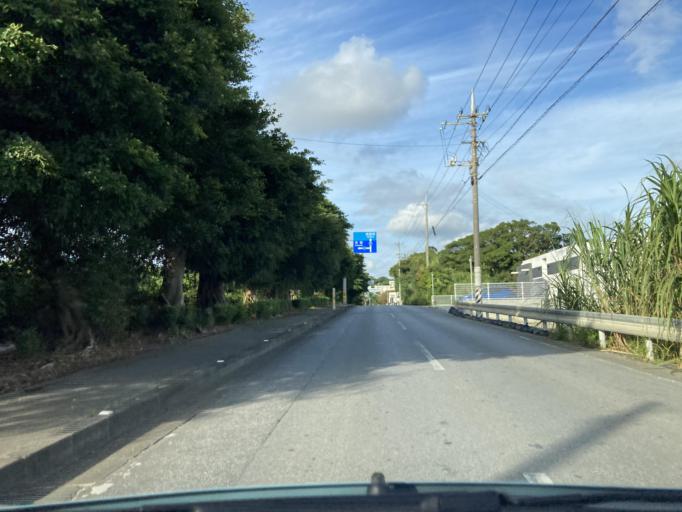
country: JP
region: Okinawa
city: Itoman
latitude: 26.1393
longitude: 127.7470
